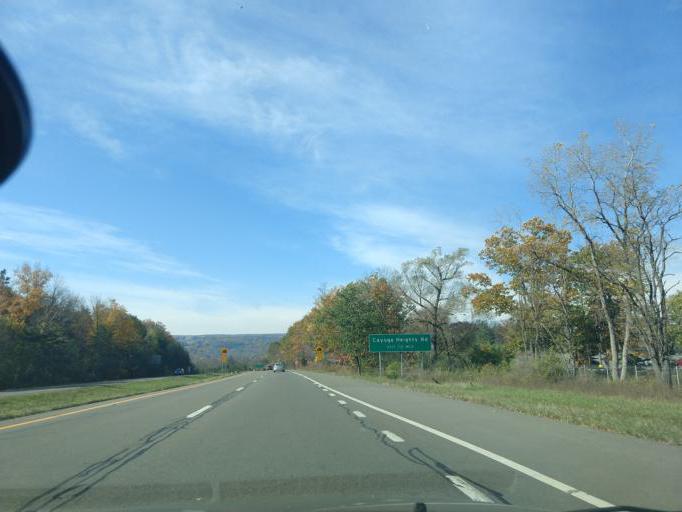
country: US
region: New York
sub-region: Tompkins County
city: Lansing
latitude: 42.4808
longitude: -76.4898
